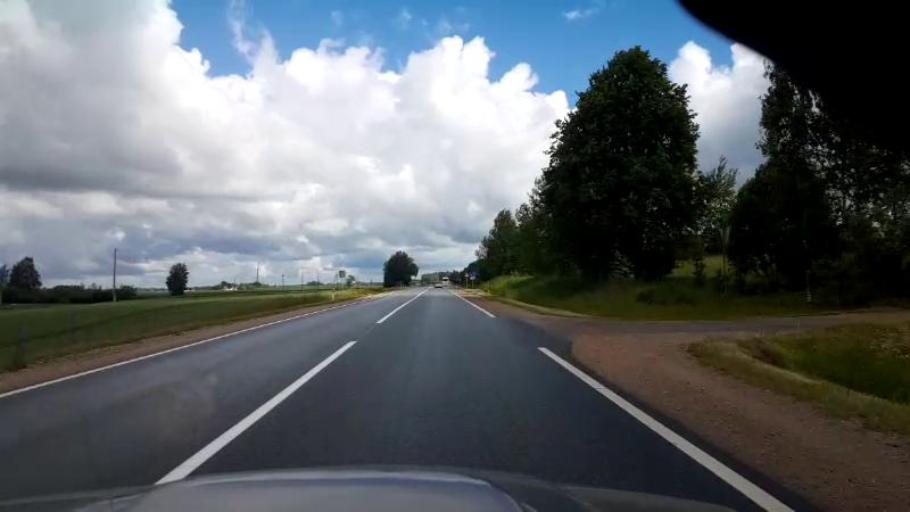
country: LV
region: Bauskas Rajons
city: Bauska
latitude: 56.5019
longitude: 24.1743
